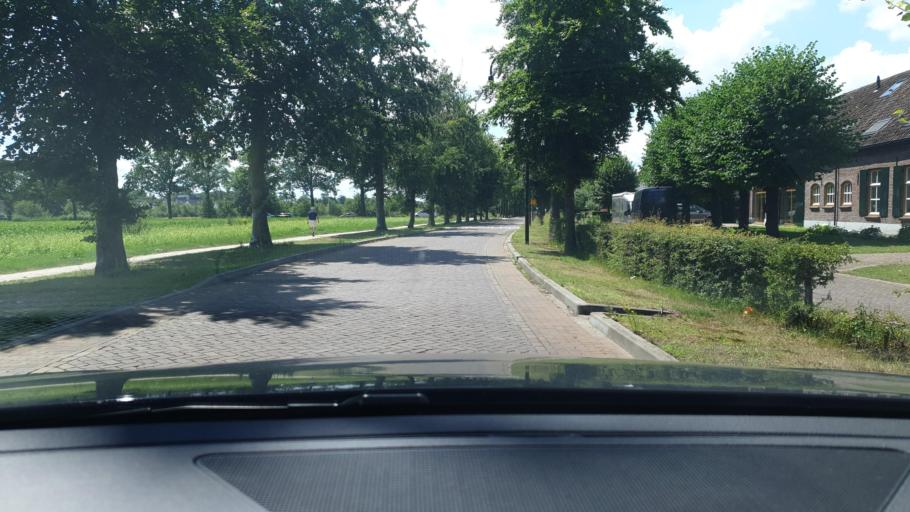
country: NL
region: North Brabant
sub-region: Gemeente Uden
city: Uden
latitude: 51.6550
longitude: 5.6061
